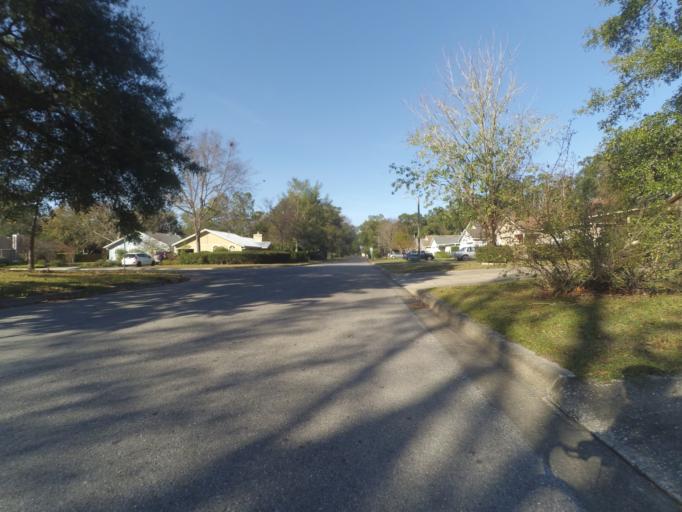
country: US
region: Florida
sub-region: Alachua County
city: Gainesville
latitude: 29.6136
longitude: -82.3651
